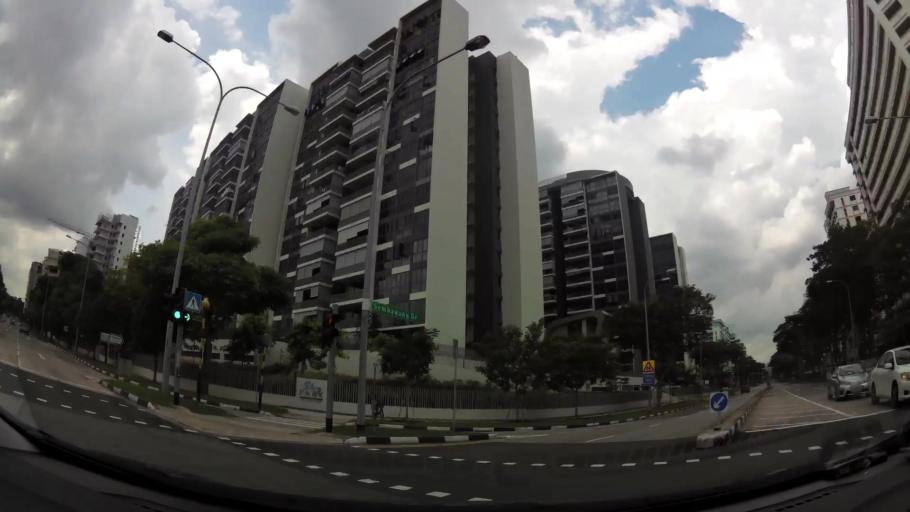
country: MY
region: Johor
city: Kampung Pasir Gudang Baru
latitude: 1.4432
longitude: 103.8208
